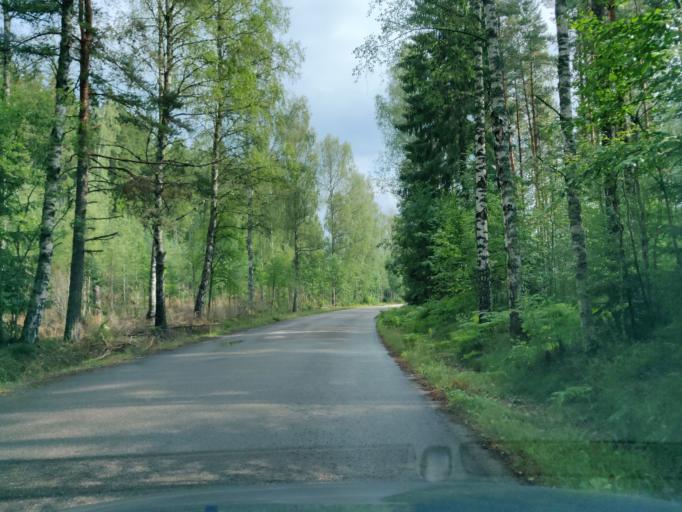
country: SE
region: Vaermland
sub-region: Hagfors Kommun
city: Hagfors
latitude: 60.0417
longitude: 13.5973
